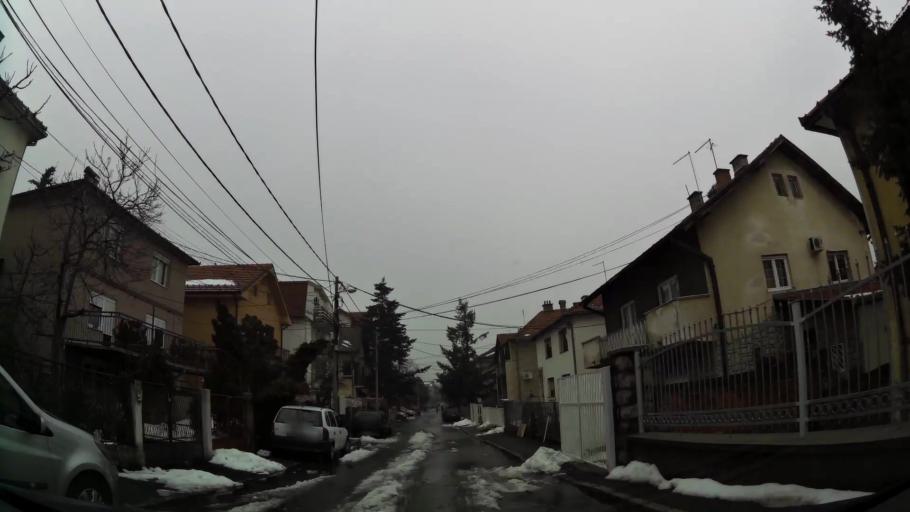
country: RS
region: Central Serbia
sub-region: Belgrade
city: Vozdovac
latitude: 44.7767
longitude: 20.4802
